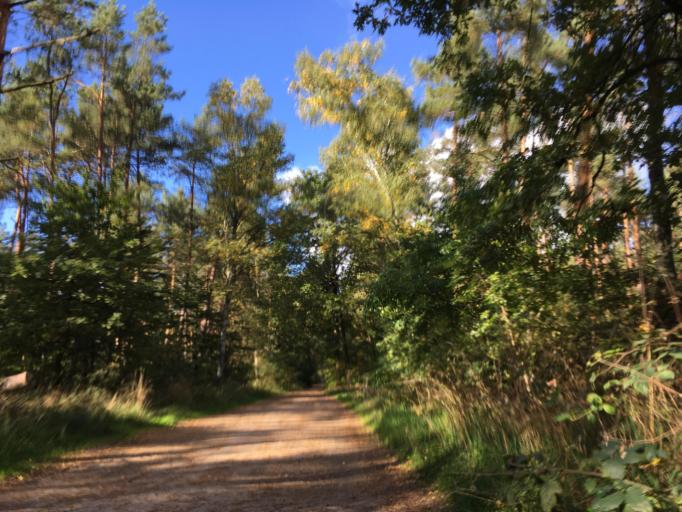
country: DE
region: Lower Saxony
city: Barendorf
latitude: 53.2214
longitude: 10.4975
